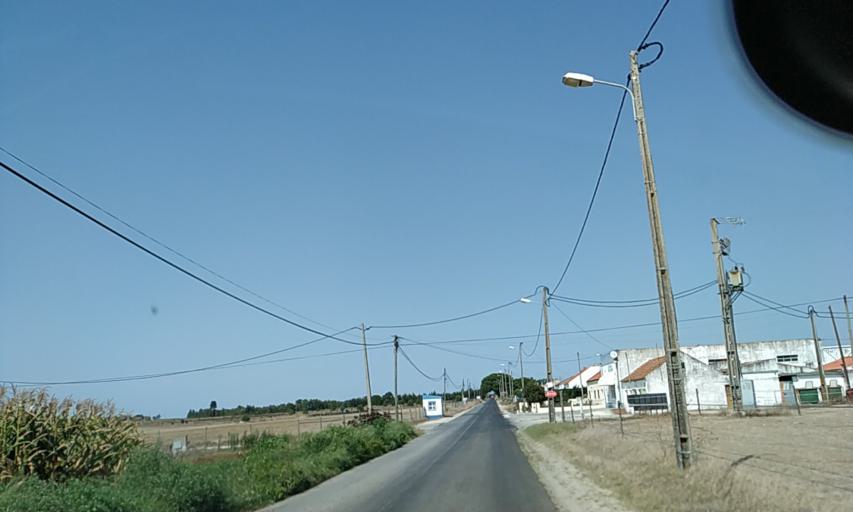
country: PT
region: Santarem
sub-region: Benavente
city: Poceirao
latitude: 38.7094
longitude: -8.7175
